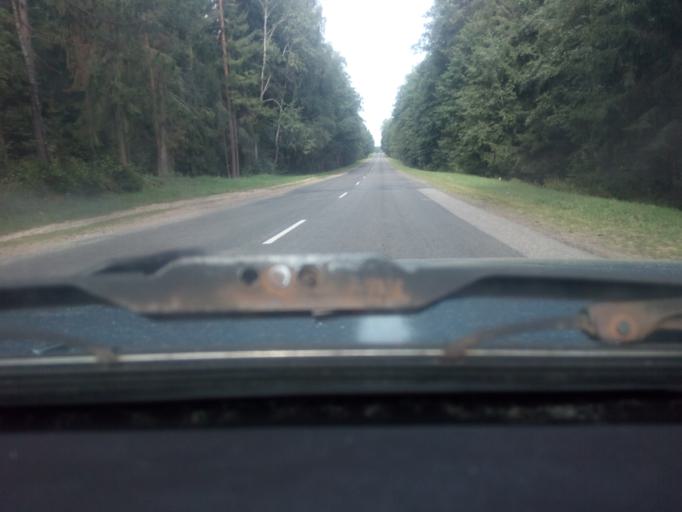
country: BY
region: Vitebsk
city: Vyerkhnyadzvinsk
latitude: 55.7946
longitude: 27.9639
